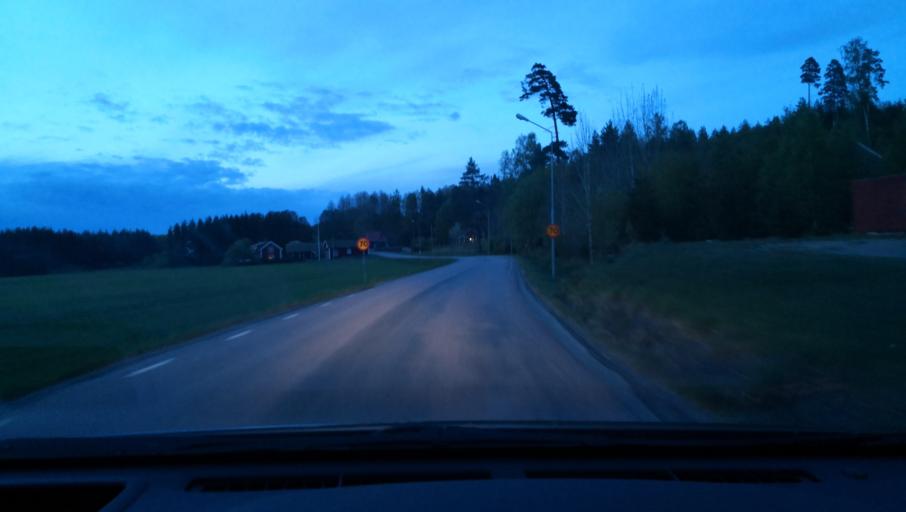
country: SE
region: OErebro
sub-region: Askersunds Kommun
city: Asbro
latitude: 59.0734
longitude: 15.0051
